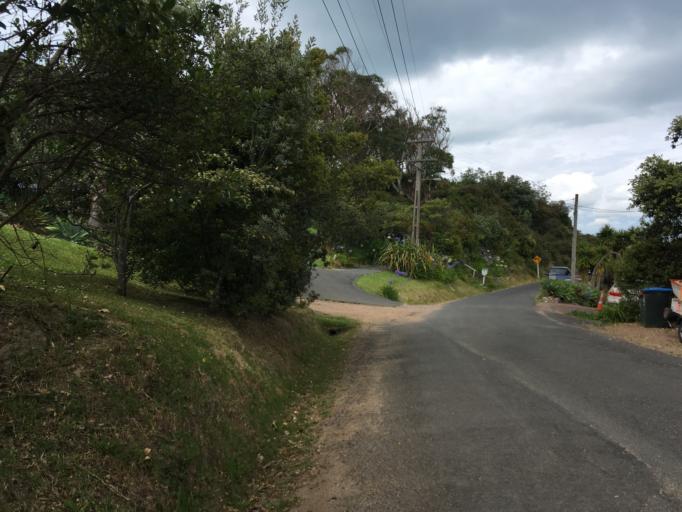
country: NZ
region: Auckland
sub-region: Auckland
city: Pakuranga
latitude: -36.7914
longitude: 175.0195
